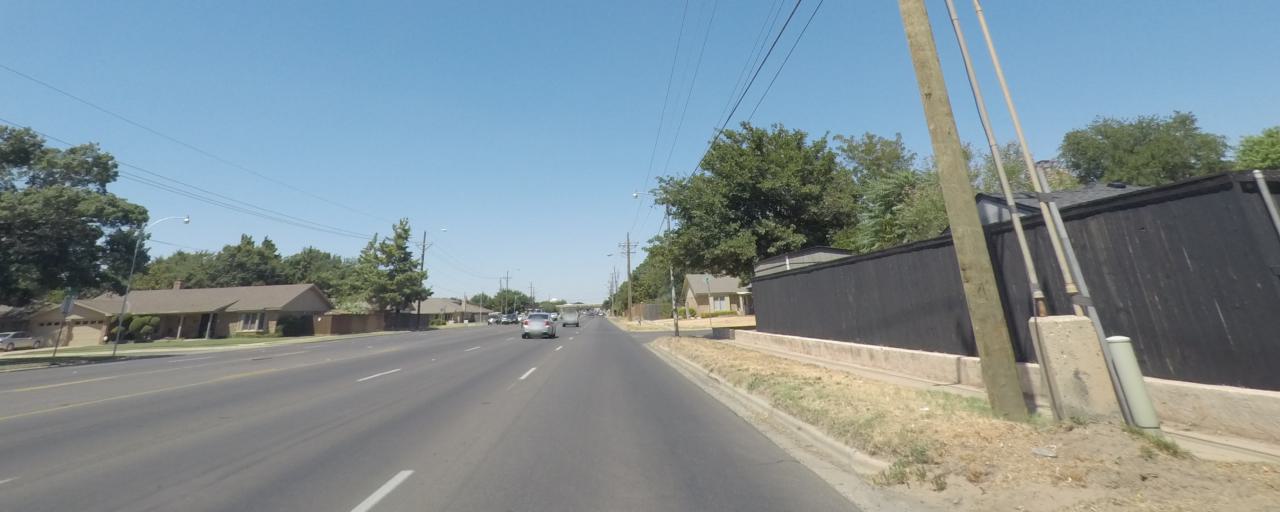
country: US
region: Texas
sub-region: Lubbock County
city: Lubbock
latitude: 33.5245
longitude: -101.8876
